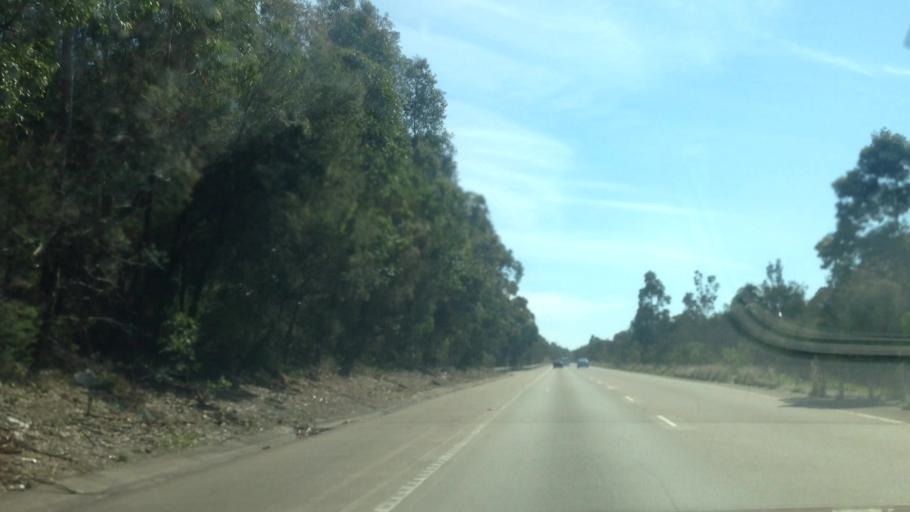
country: AU
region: New South Wales
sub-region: Lake Macquarie Shire
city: Fennell Bay
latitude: -32.9673
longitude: 151.5359
